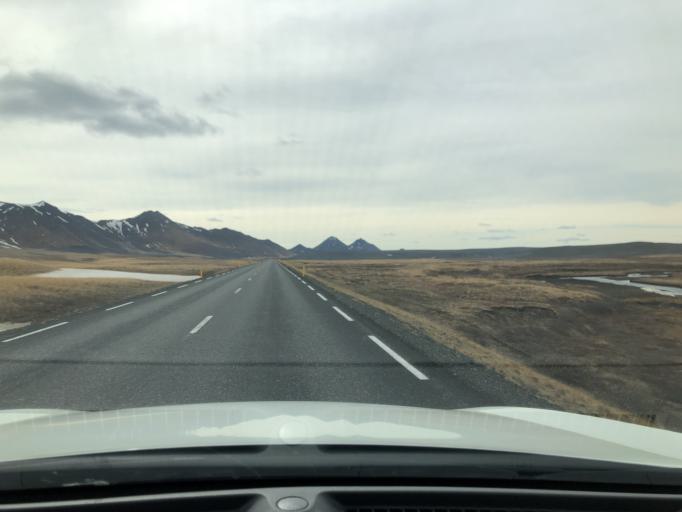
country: IS
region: Northeast
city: Laugar
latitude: 65.5076
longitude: -15.9797
